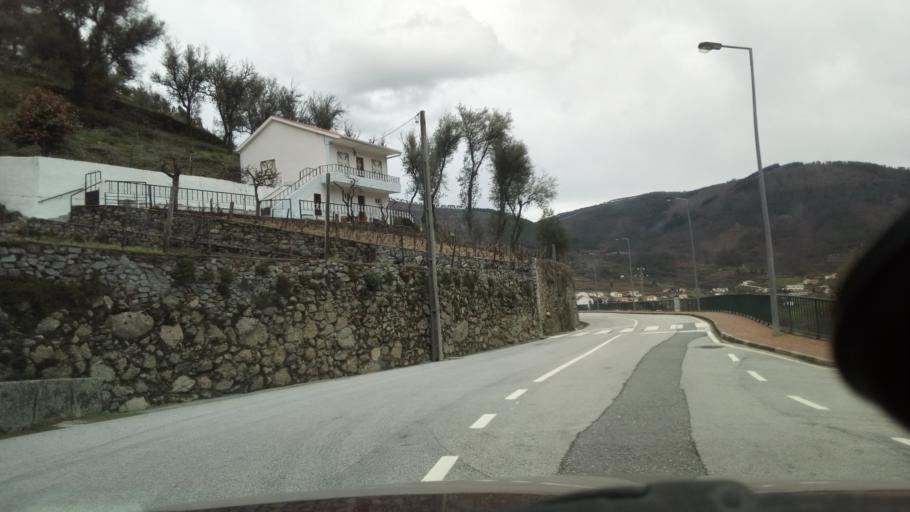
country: PT
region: Guarda
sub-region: Manteigas
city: Manteigas
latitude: 40.3948
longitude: -7.5433
